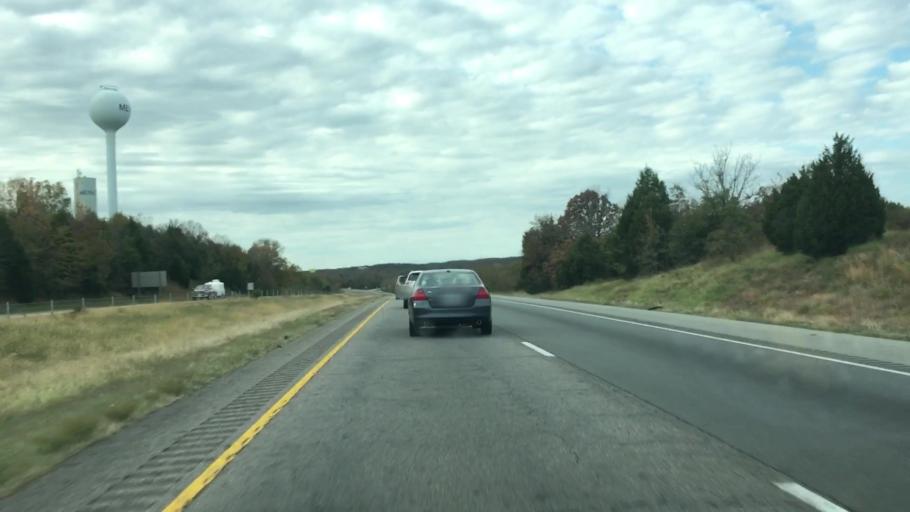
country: US
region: Arkansas
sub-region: Faulkner County
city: Conway
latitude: 35.1477
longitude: -92.5403
